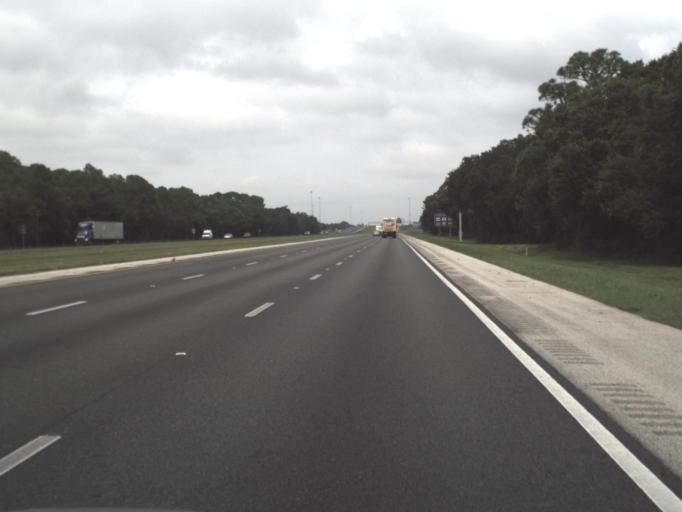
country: US
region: Florida
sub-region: Manatee County
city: Ellenton
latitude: 27.4796
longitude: -82.4663
